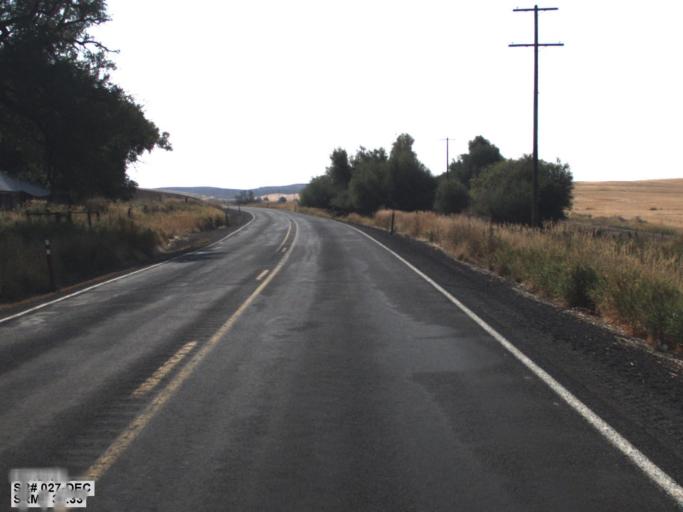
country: US
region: Washington
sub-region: Whitman County
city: Colfax
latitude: 47.1167
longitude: -117.1921
